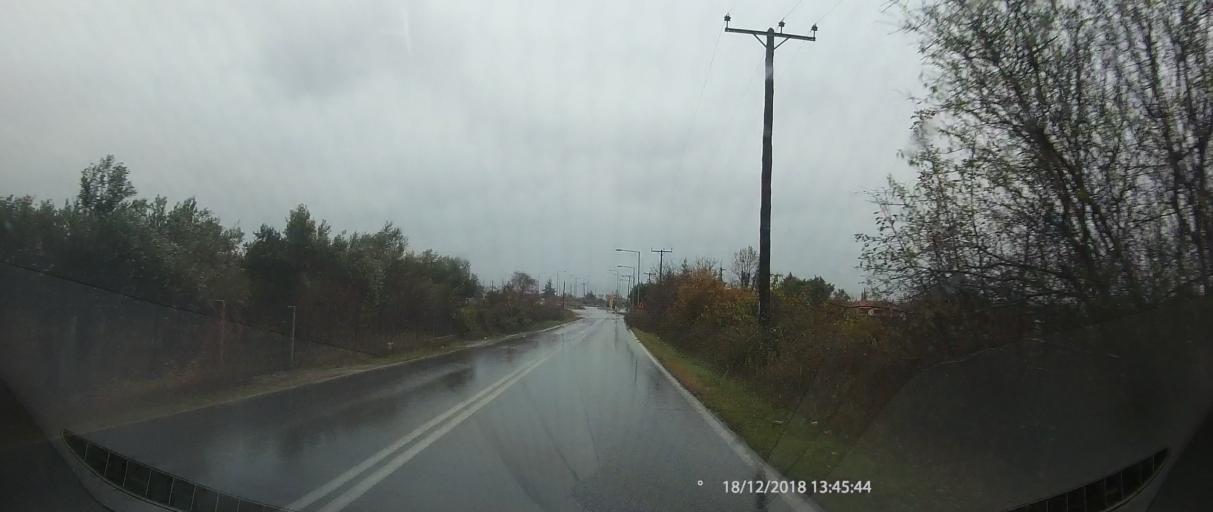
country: GR
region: Central Macedonia
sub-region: Nomos Pierias
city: Leptokarya
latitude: 40.0985
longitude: 22.5500
